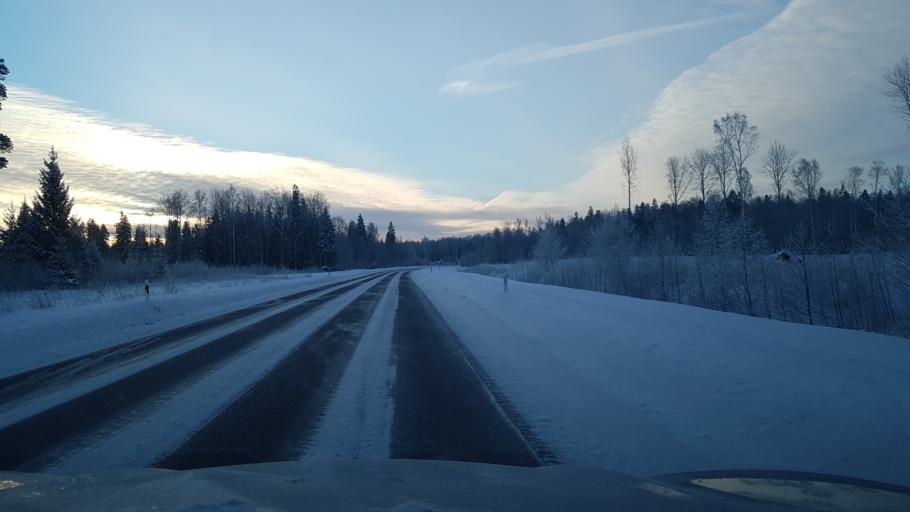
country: EE
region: Ida-Virumaa
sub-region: Johvi vald
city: Johvi
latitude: 59.3545
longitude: 27.4660
